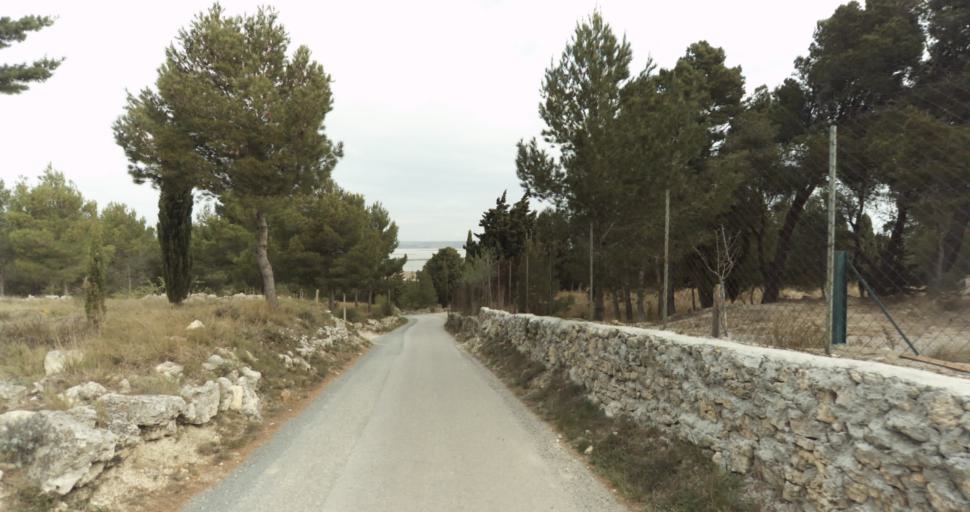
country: FR
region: Languedoc-Roussillon
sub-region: Departement de l'Aude
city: Leucate
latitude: 42.9322
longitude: 3.0235
